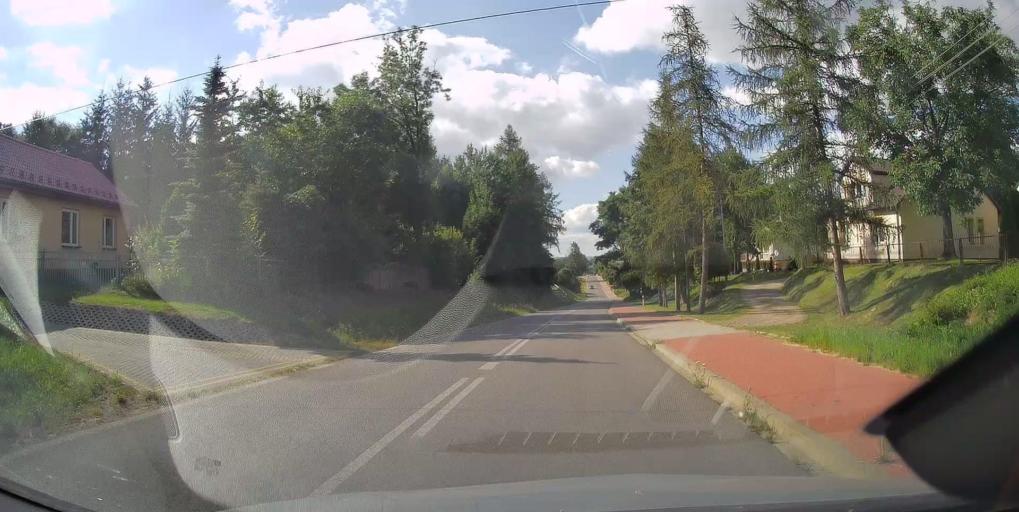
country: PL
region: Swietokrzyskie
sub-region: Powiat kielecki
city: Nowa Slupia
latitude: 50.8722
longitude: 21.0738
